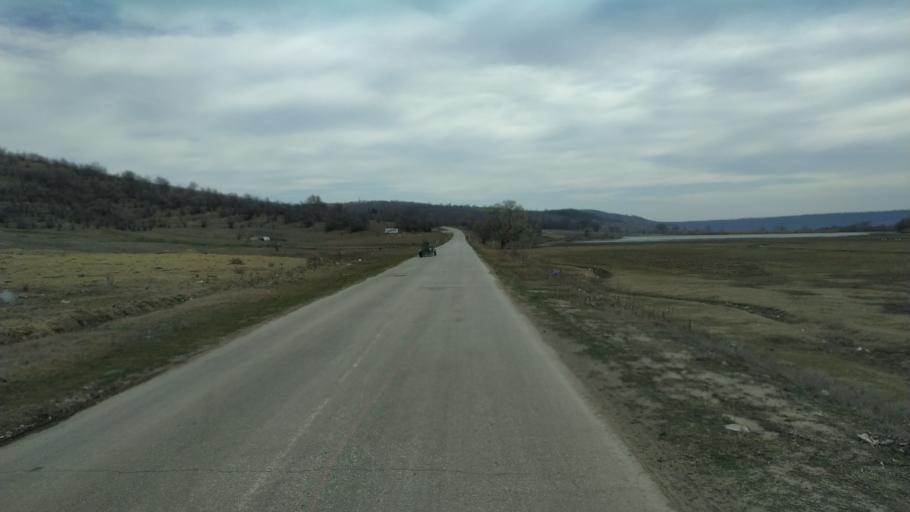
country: MD
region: Nisporeni
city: Nisporeni
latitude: 46.9595
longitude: 28.2188
